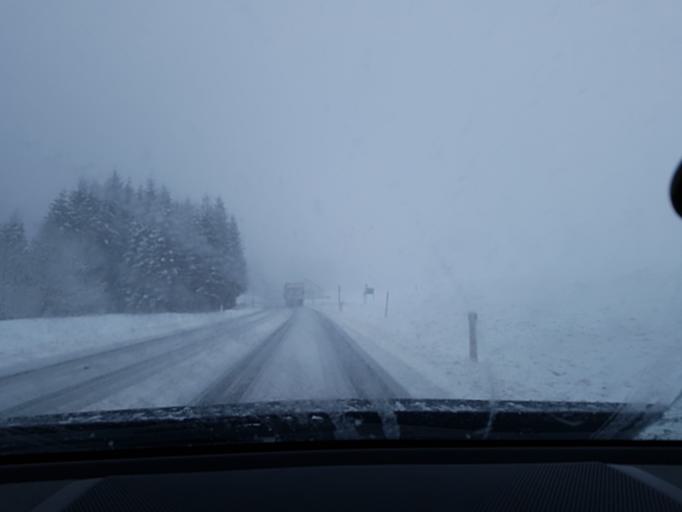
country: AT
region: Salzburg
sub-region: Politischer Bezirk Hallein
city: Abtenau
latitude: 47.5783
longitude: 13.3248
